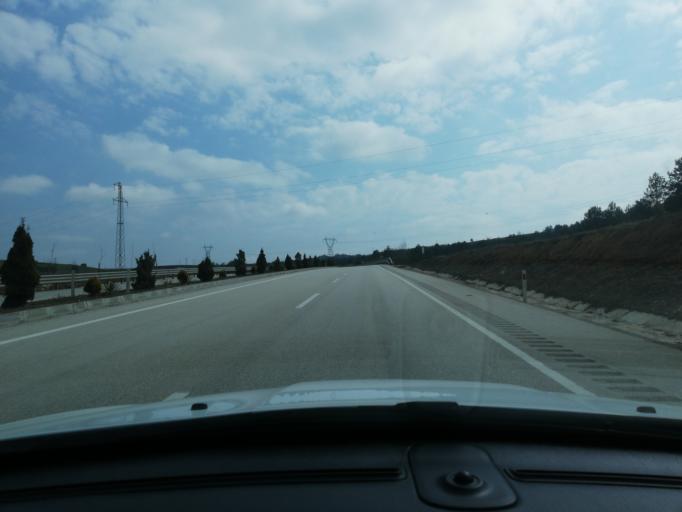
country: TR
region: Kastamonu
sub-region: Cide
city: Kastamonu
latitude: 41.3750
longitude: 33.7951
